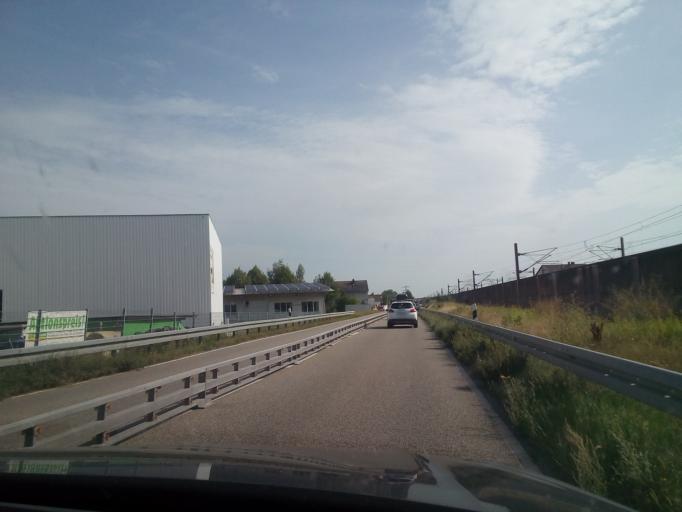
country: DE
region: Baden-Wuerttemberg
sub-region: Karlsruhe Region
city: Sinzheim
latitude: 48.7642
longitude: 8.1622
